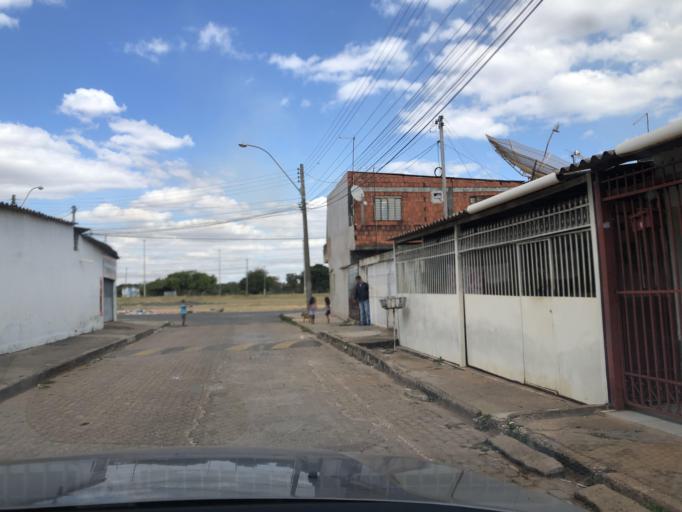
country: BR
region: Federal District
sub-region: Brasilia
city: Brasilia
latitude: -15.8942
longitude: -48.1405
